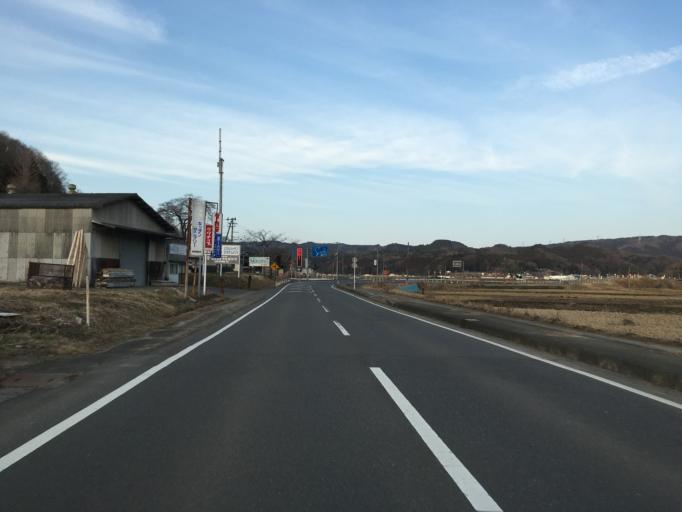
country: JP
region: Ibaraki
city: Daigo
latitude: 36.8612
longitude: 140.4137
